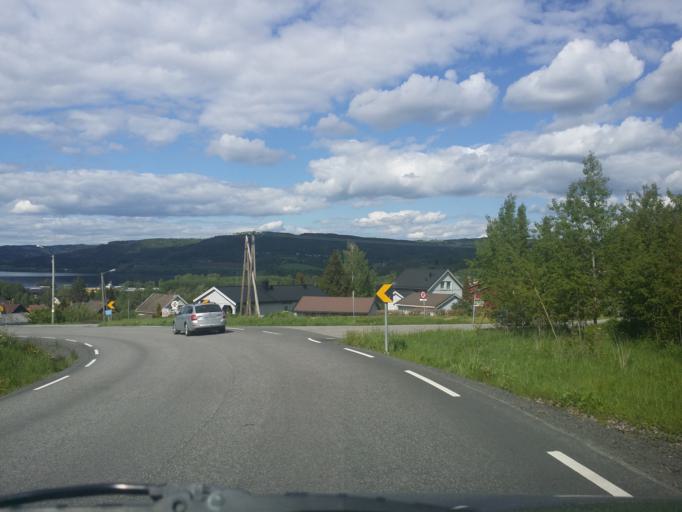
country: NO
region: Oppland
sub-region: Jevnaker
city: Jevnaker
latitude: 60.2353
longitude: 10.4066
